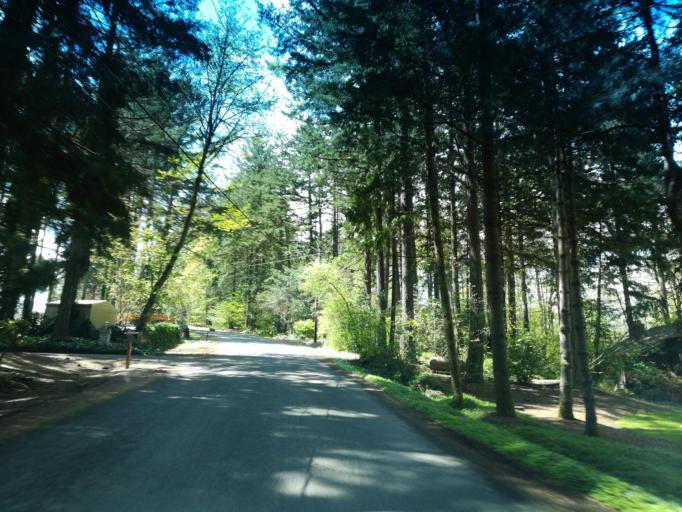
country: US
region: Oregon
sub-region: Clackamas County
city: Damascus
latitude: 45.4430
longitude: -122.4599
